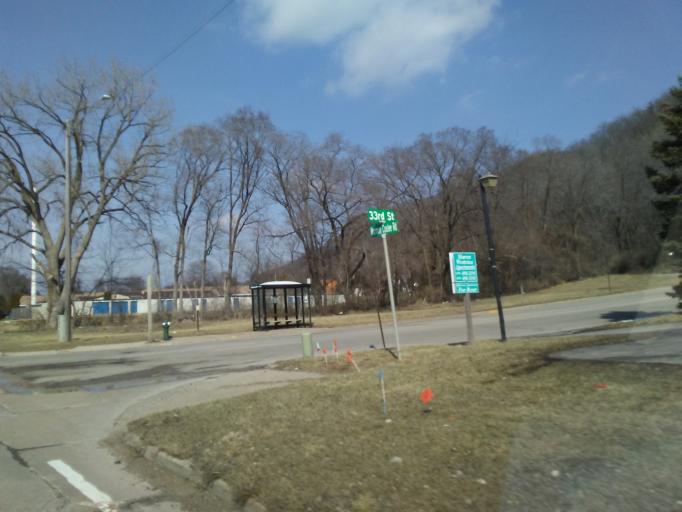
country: US
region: Wisconsin
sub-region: La Crosse County
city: La Crosse
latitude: 43.7565
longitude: -91.2041
